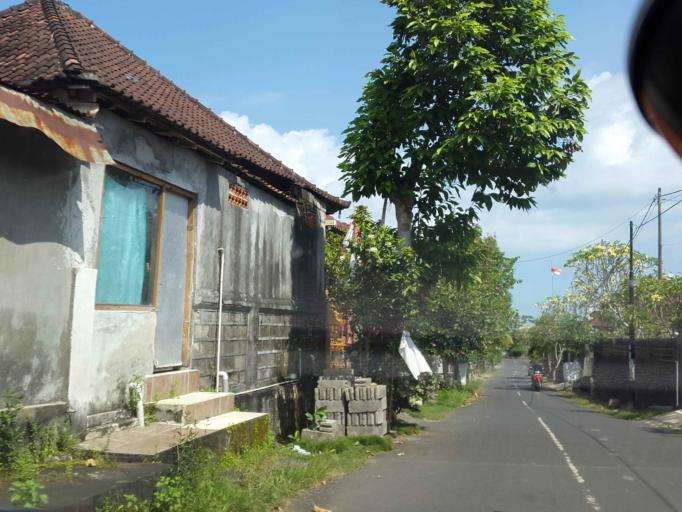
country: ID
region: Bali
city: Klungkung
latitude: -8.5449
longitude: 115.3778
